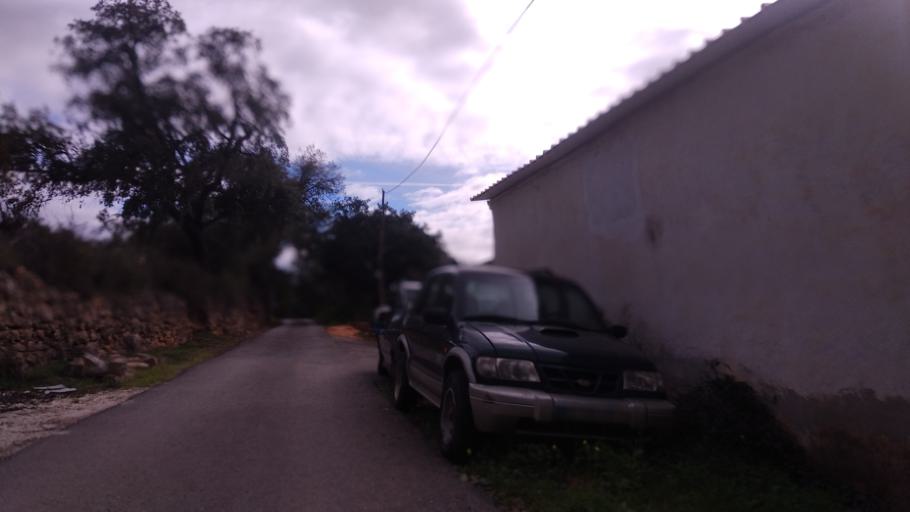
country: PT
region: Faro
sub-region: Loule
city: Almancil
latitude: 37.0994
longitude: -8.0480
